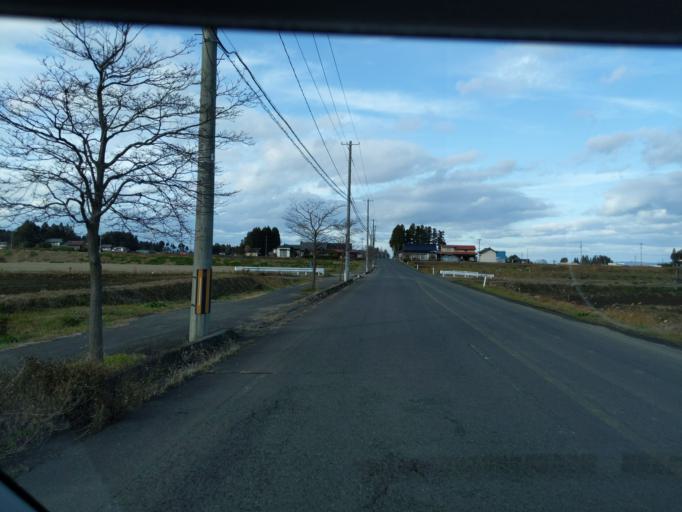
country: JP
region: Iwate
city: Mizusawa
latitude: 39.1207
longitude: 141.0925
